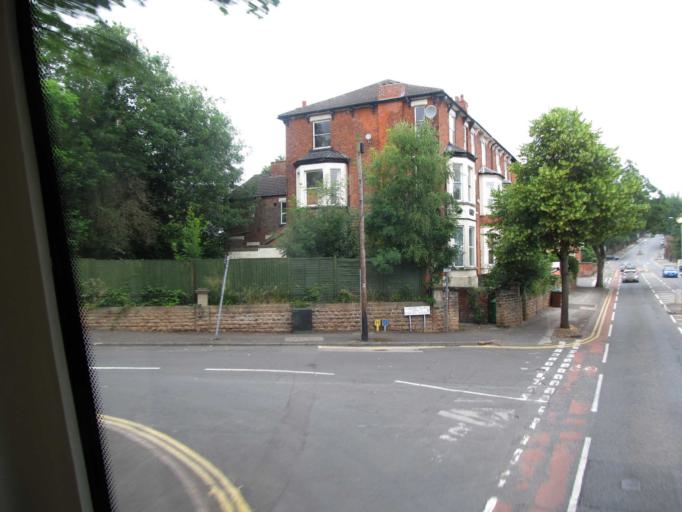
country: GB
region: England
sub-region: Nottingham
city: Nottingham
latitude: 52.9686
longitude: -1.1426
